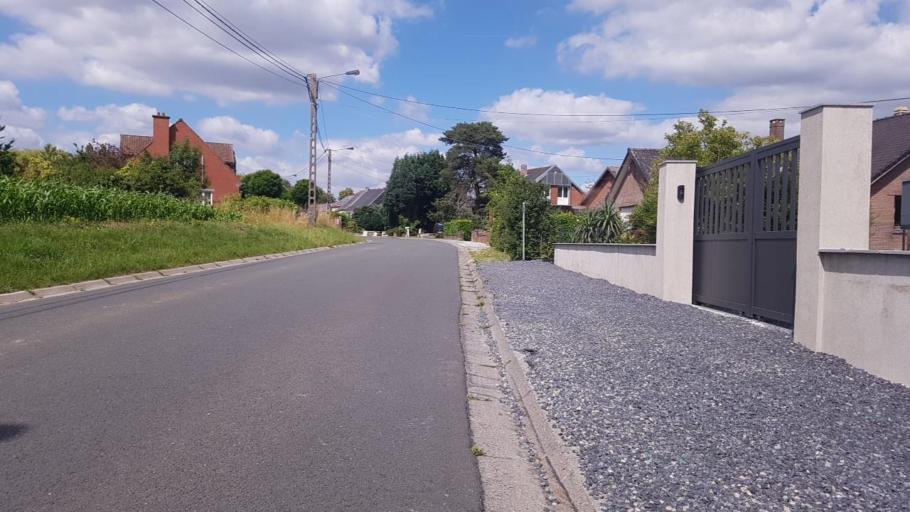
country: BE
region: Wallonia
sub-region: Province du Hainaut
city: Charleroi
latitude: 50.3381
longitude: 4.3927
